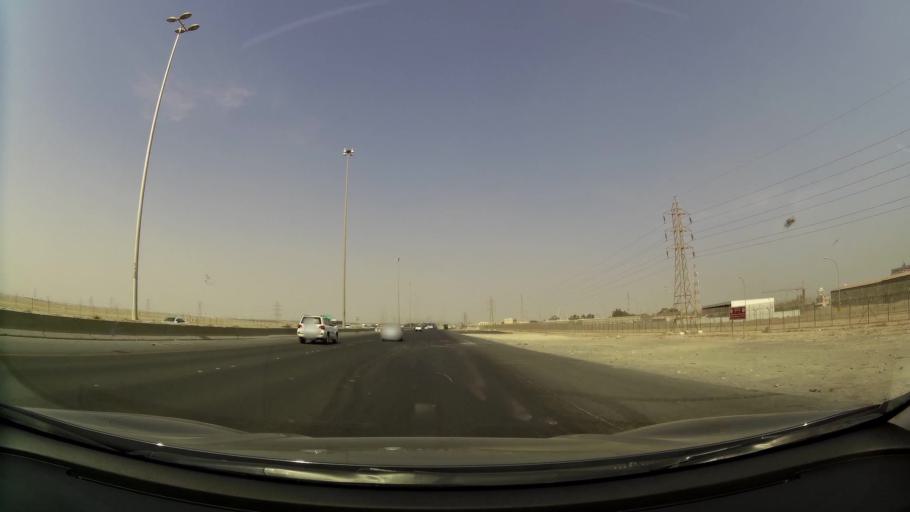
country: KW
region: Al Ahmadi
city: Al Fahahil
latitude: 29.0303
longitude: 48.1222
